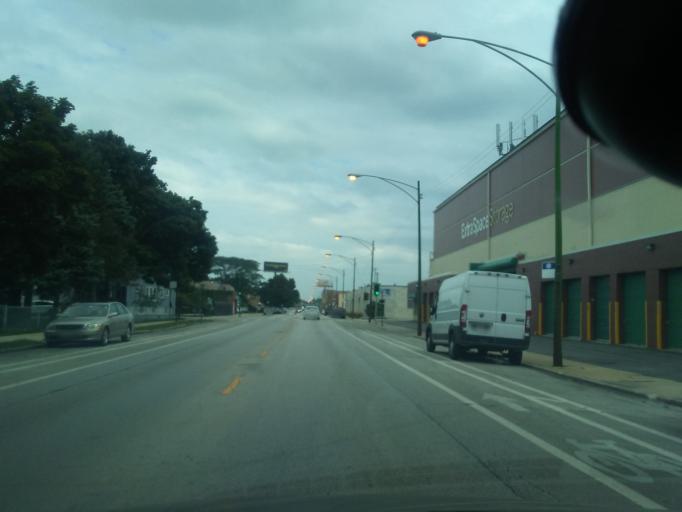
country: US
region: Illinois
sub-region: Cook County
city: Harwood Heights
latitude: 41.9780
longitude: -87.7738
